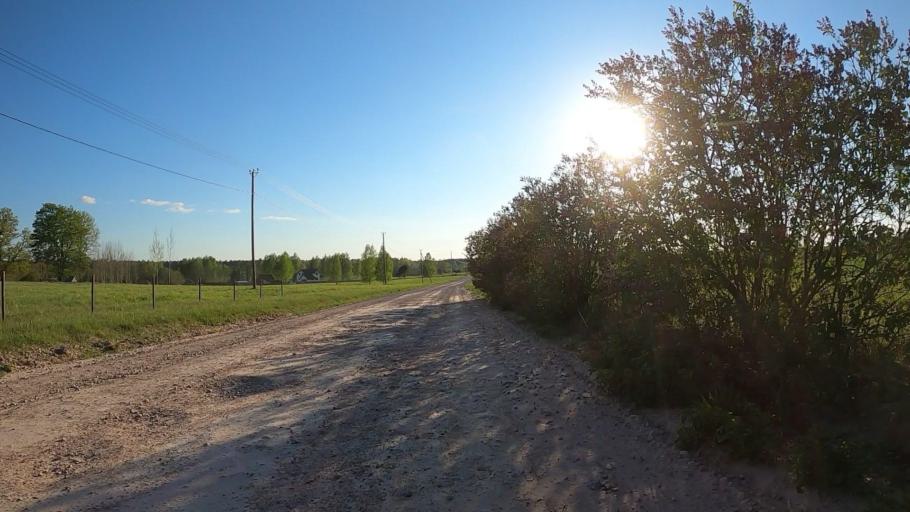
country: LV
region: Kekava
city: Kekava
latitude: 56.7575
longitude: 24.2582
